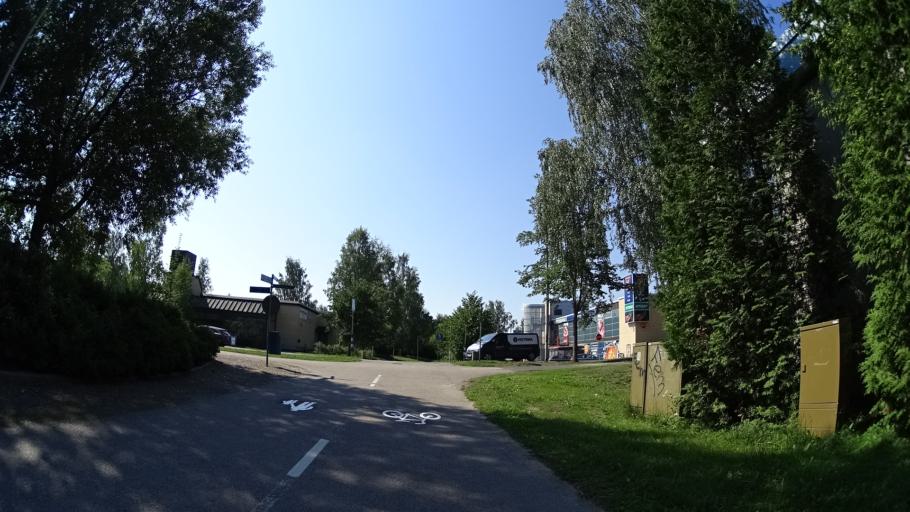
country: FI
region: Uusimaa
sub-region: Helsinki
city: Kerava
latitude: 60.3810
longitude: 25.0929
